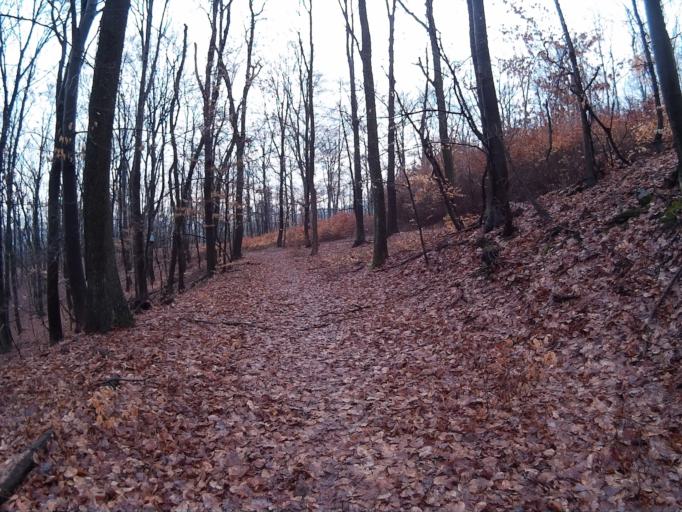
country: HU
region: Borsod-Abauj-Zemplen
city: Satoraljaujhely
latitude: 48.4160
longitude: 21.5919
